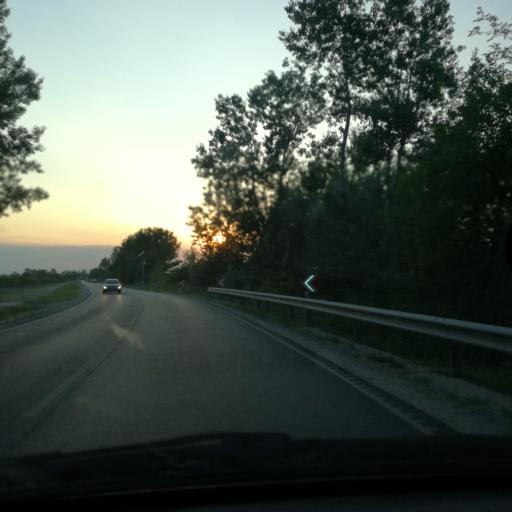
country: HU
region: Bacs-Kiskun
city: Soltvadkert
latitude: 46.5854
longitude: 19.3608
